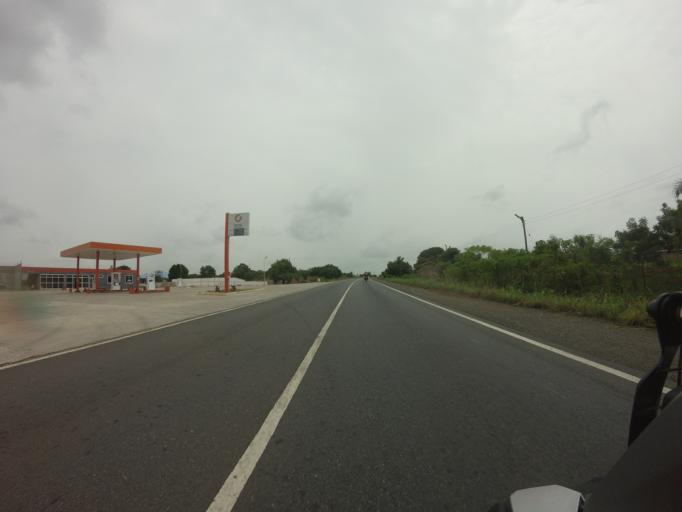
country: GH
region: Volta
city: Keta
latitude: 6.1146
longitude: 0.7962
